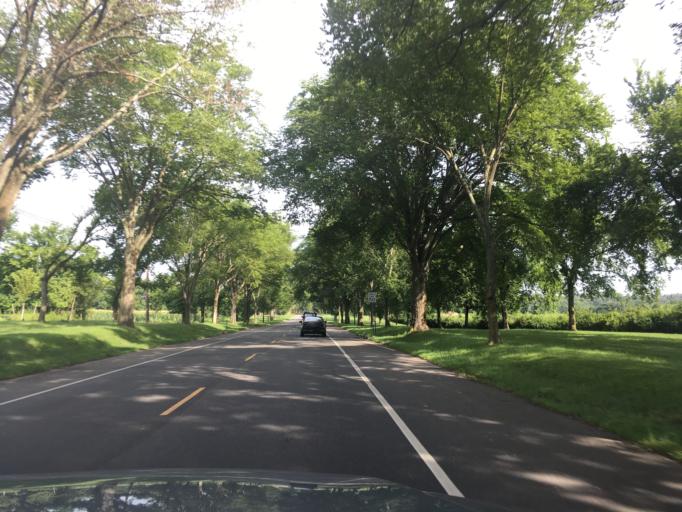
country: US
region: New Jersey
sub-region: Mercer County
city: Princeton
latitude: 40.3331
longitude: -74.6401
